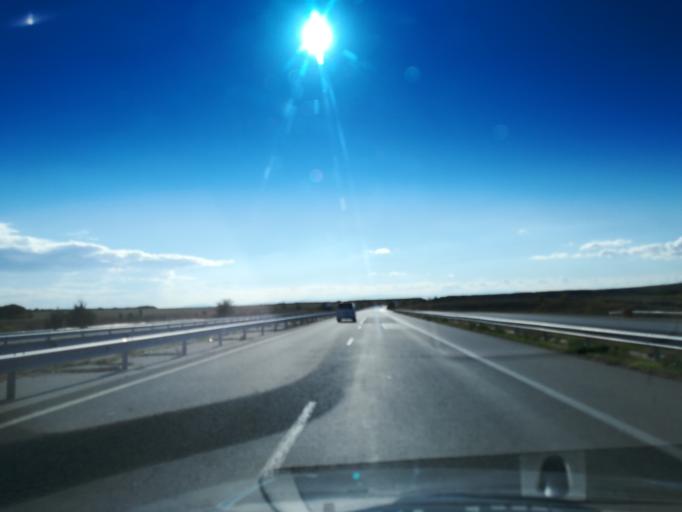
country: BG
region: Stara Zagora
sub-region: Obshtina Nikolaevo
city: Elkhovo
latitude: 42.2874
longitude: 25.4635
